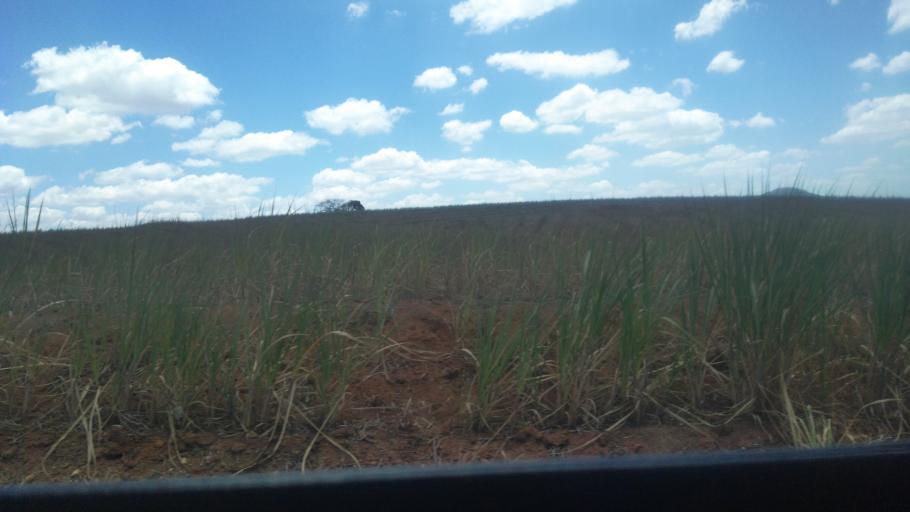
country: BR
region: Pernambuco
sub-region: Nazare Da Mata
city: Nazare da Mata
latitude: -7.7352
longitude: -35.2738
